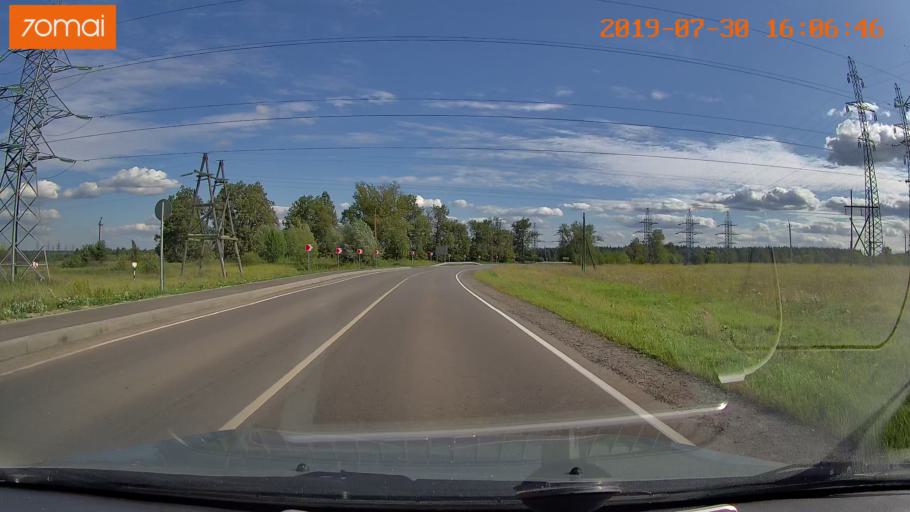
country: RU
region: Moskovskaya
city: Peski
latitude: 55.2527
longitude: 38.7192
